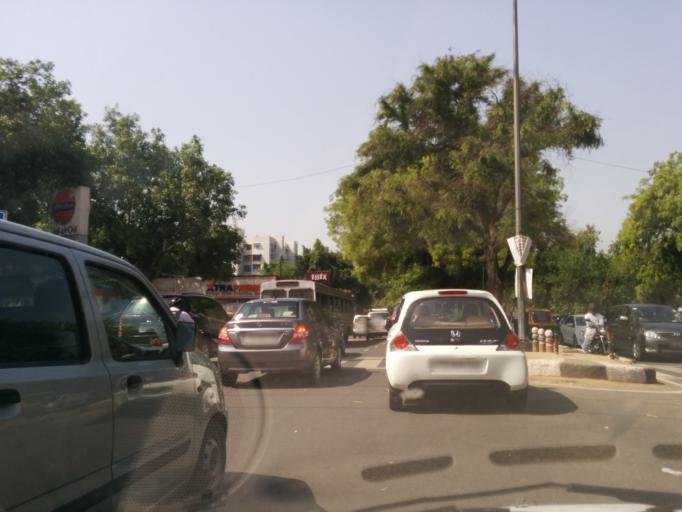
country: IN
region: NCT
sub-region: New Delhi
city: New Delhi
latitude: 28.5445
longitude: 77.2014
